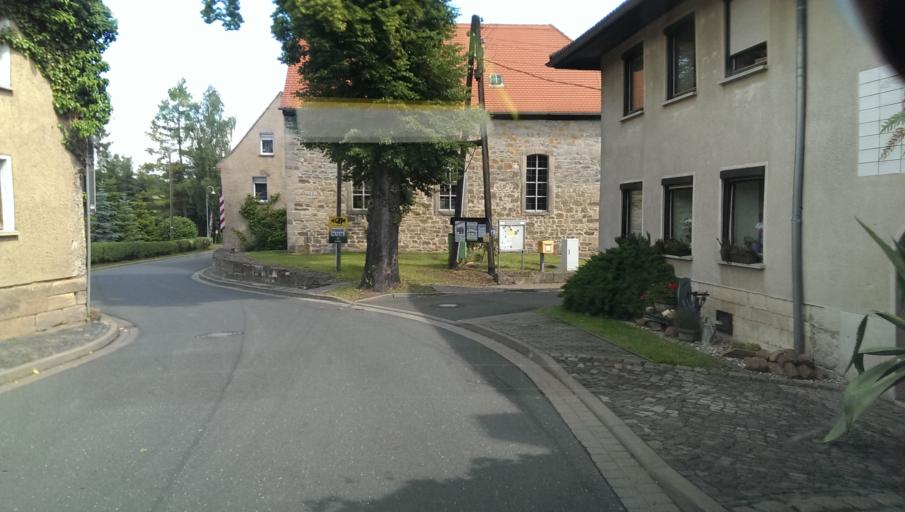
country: DE
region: Saxony-Anhalt
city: Bad Bibra
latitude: 51.1738
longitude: 11.5732
